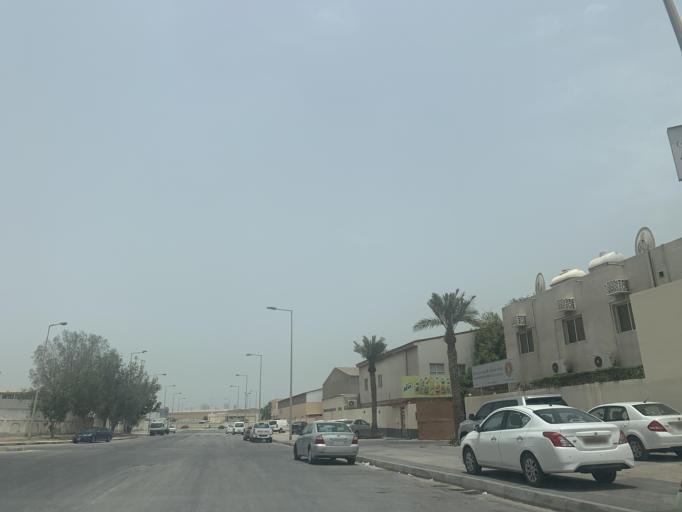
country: BH
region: Northern
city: Sitrah
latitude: 26.1806
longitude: 50.6098
